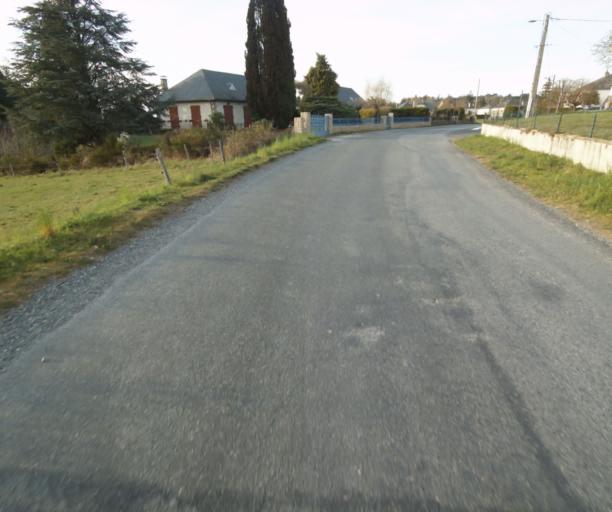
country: FR
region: Limousin
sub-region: Departement de la Correze
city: Correze
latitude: 45.3751
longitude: 1.8651
